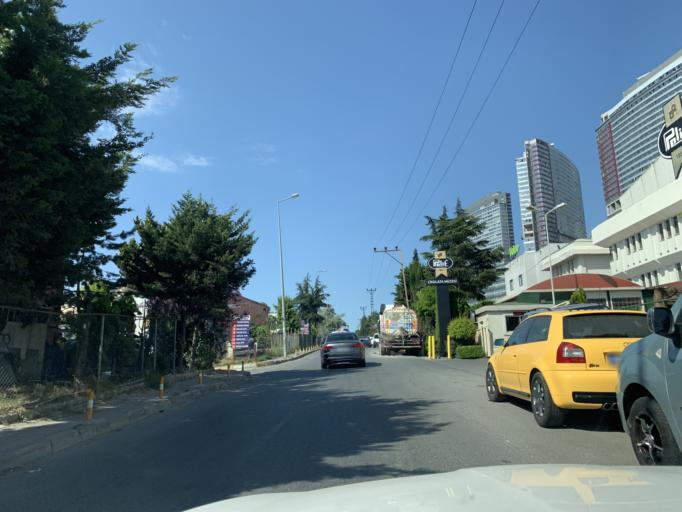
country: TR
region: Istanbul
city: Esenyurt
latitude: 41.0596
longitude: 28.6616
